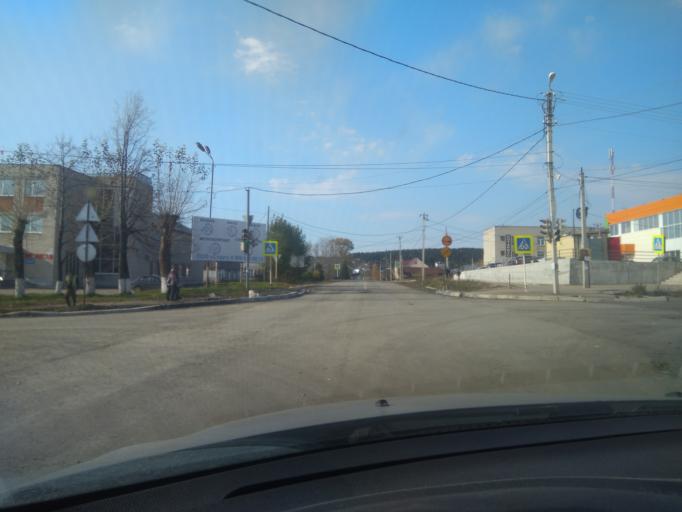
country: RU
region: Sverdlovsk
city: Nizhniye Sergi
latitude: 56.6621
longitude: 59.2995
